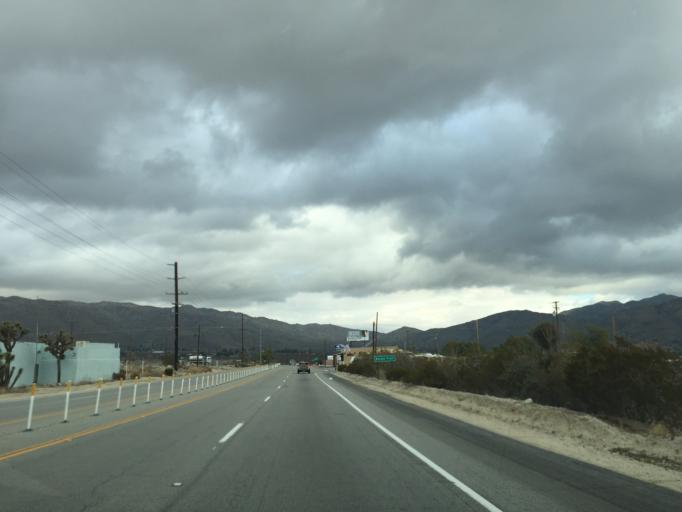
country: US
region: California
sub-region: San Bernardino County
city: Morongo Valley
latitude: 34.0769
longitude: -116.5405
